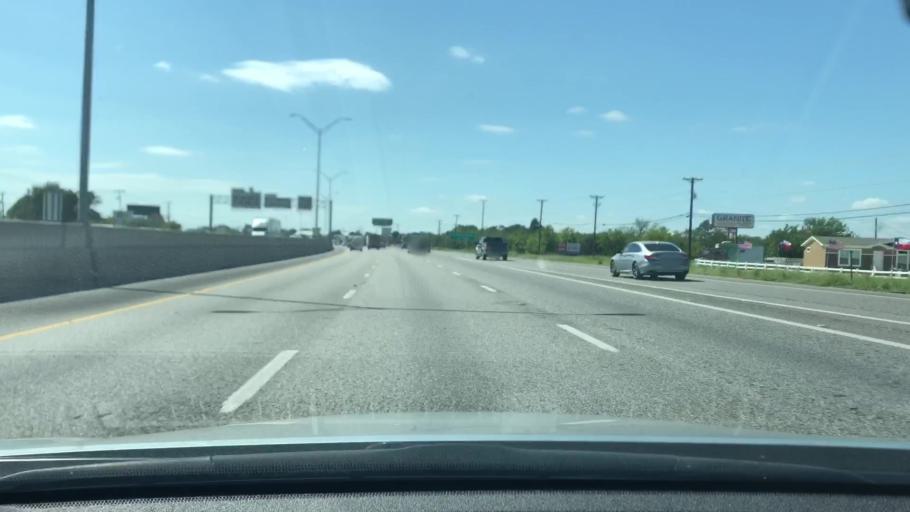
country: US
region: Texas
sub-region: Comal County
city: New Braunfels
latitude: 29.7245
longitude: -98.0839
